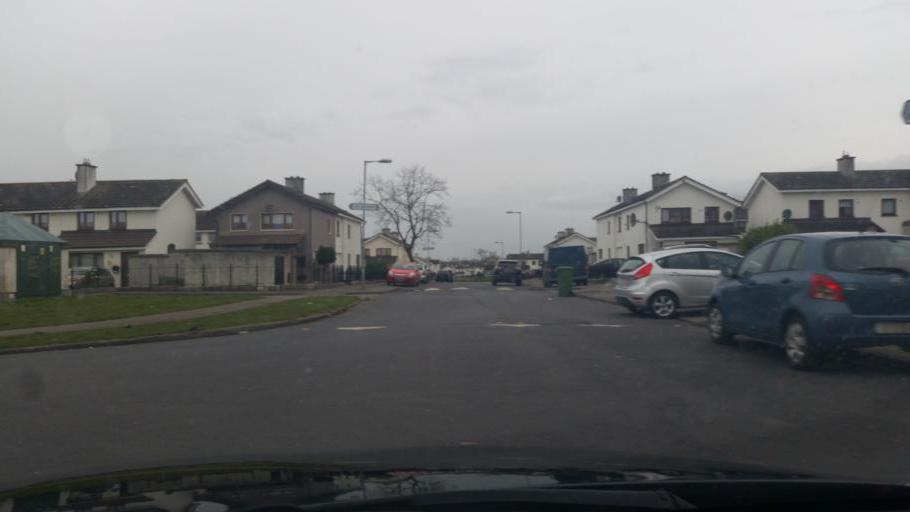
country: IE
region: Leinster
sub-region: Fingal County
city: Blanchardstown
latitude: 53.4005
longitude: -6.3771
